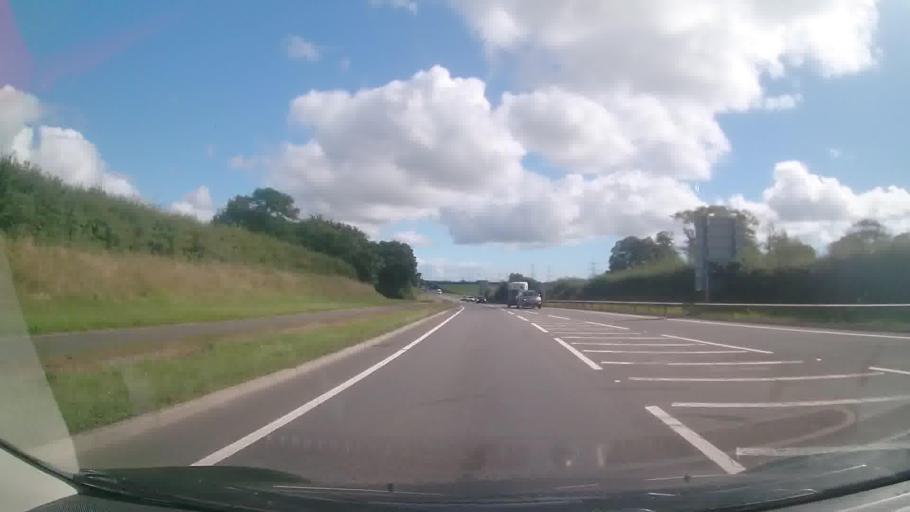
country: GB
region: Wales
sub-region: Pembrokeshire
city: Pembroke
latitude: 51.6890
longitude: -4.8648
